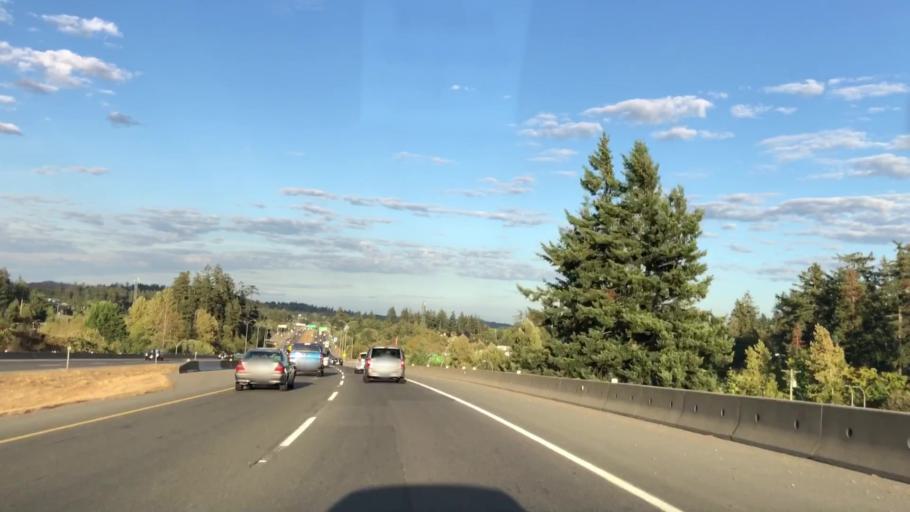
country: CA
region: British Columbia
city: Colwood
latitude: 48.4639
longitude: -123.4563
